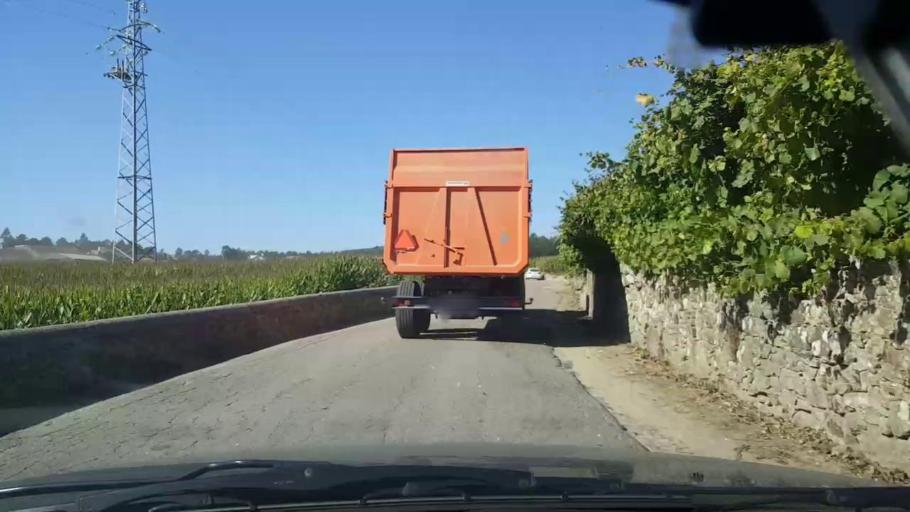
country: PT
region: Braga
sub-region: Vila Nova de Famalicao
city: Ribeirao
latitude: 41.3596
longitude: -8.6433
